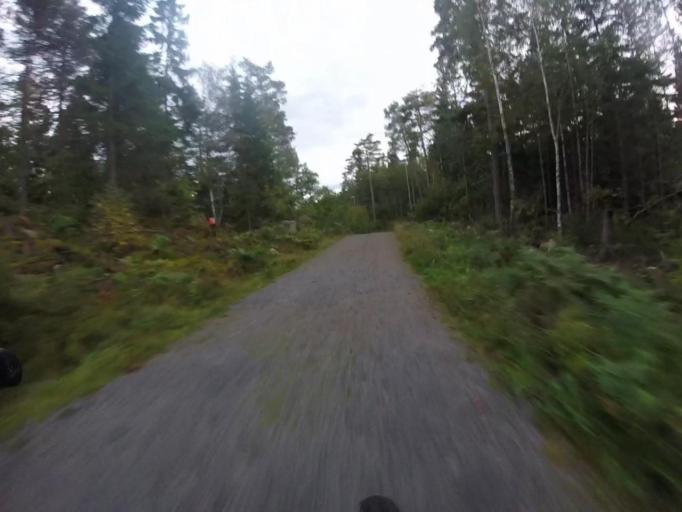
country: SE
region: Vaestra Goetaland
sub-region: Trollhattan
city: Trollhattan
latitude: 58.2905
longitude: 12.2617
